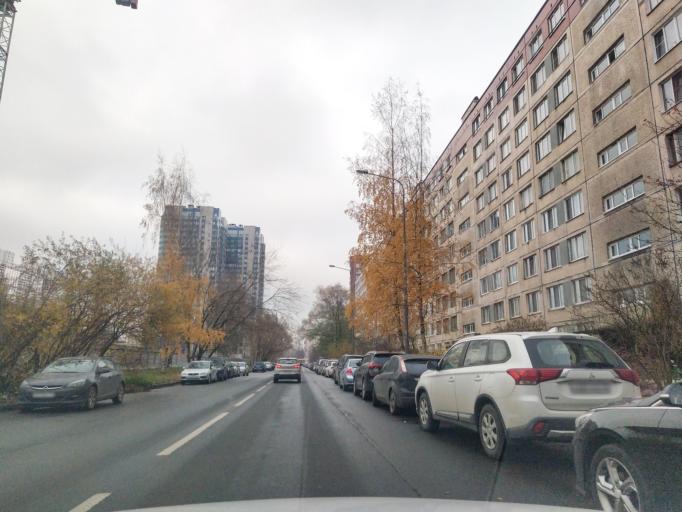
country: RU
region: Leningrad
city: Parnas
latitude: 60.0445
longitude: 30.3650
